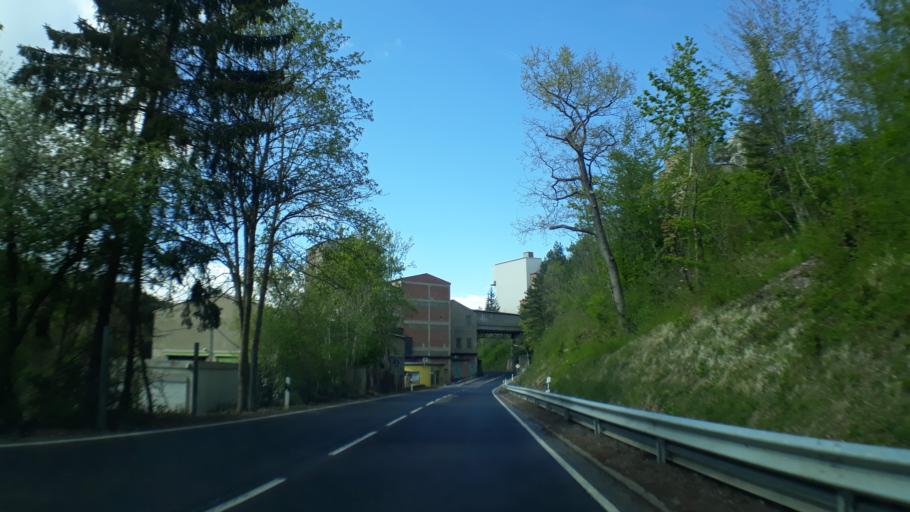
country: DE
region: North Rhine-Westphalia
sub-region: Regierungsbezirk Koln
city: Kall
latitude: 50.5194
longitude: 6.5596
